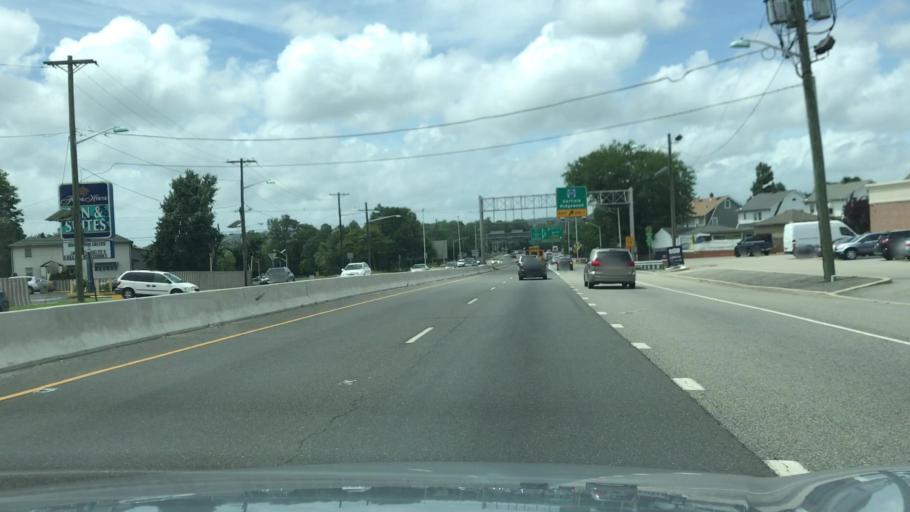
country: US
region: New Jersey
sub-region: Bergen County
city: Elmwood Park
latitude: 40.8934
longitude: -74.1240
